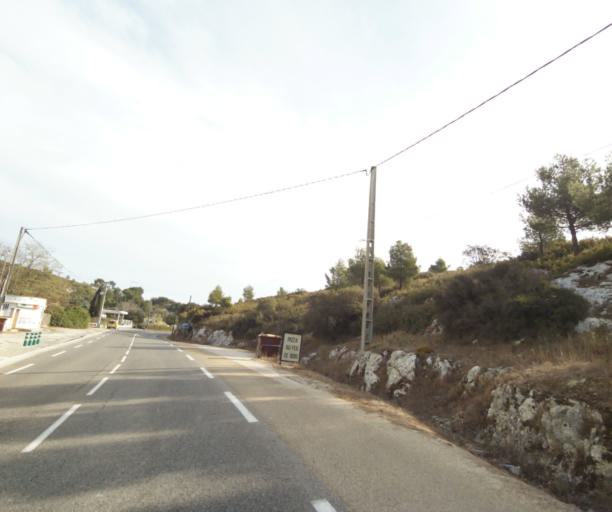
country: FR
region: Provence-Alpes-Cote d'Azur
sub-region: Departement des Bouches-du-Rhone
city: Ensues-la-Redonne
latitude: 43.3566
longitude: 5.2157
